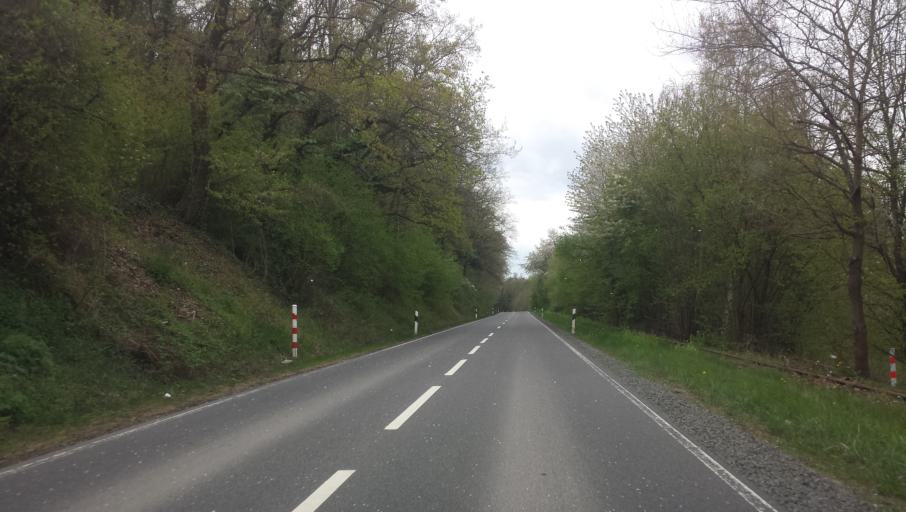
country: DE
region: Rheinland-Pfalz
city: Wendelsheim
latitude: 49.7727
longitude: 8.0171
